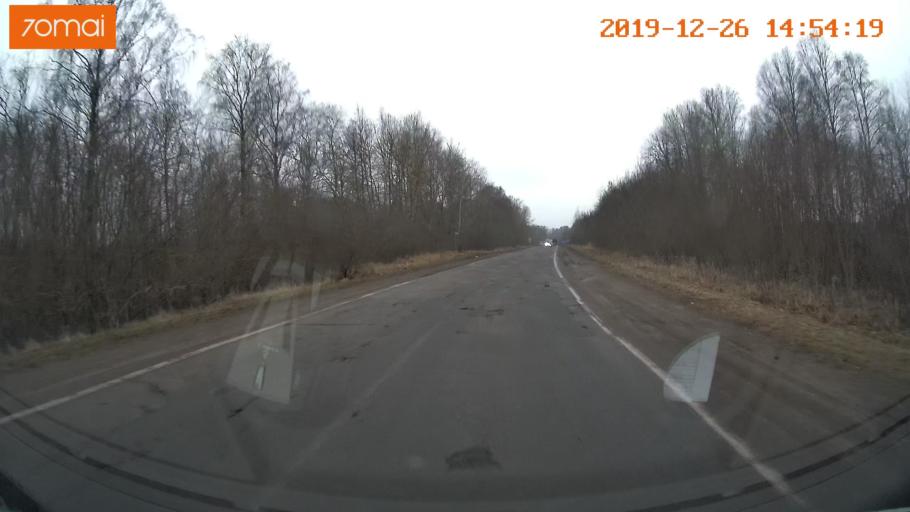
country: RU
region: Jaroslavl
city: Rybinsk
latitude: 58.3081
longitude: 38.8854
